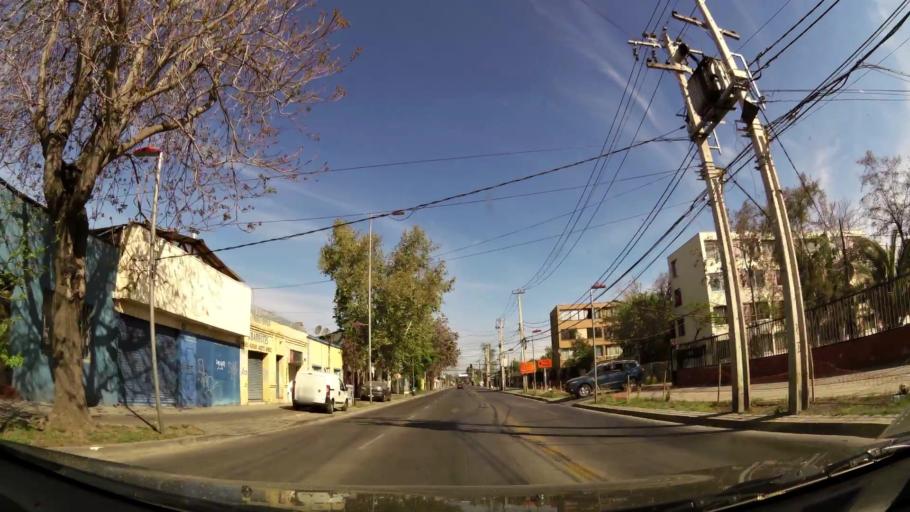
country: CL
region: Santiago Metropolitan
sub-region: Provincia de Santiago
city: Santiago
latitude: -33.4757
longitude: -70.6348
